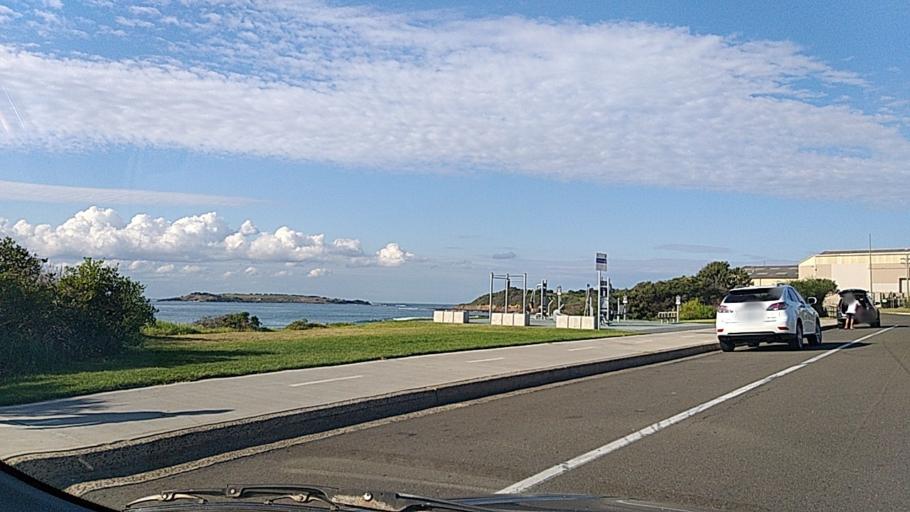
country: AU
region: New South Wales
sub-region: Wollongong
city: Port Kembla
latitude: -34.4813
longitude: 150.9129
